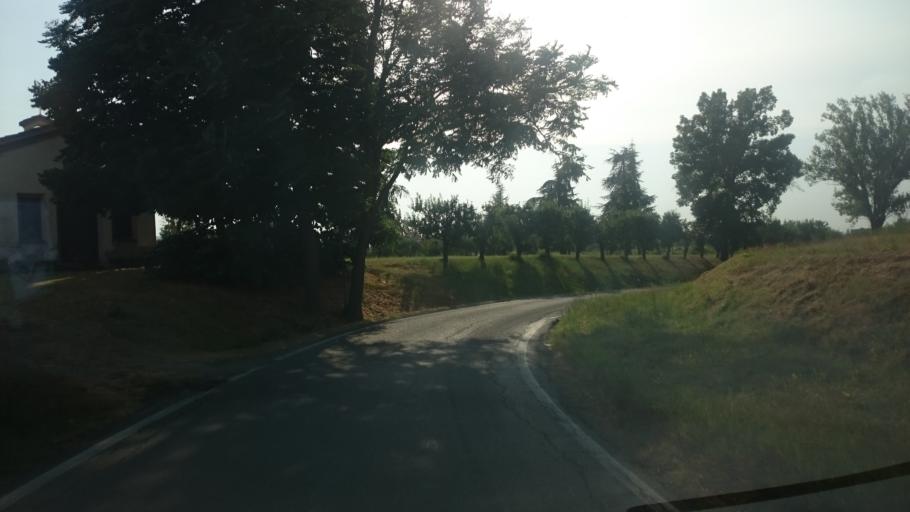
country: IT
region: Emilia-Romagna
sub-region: Provincia di Reggio Emilia
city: Arceto
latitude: 44.5994
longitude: 10.7171
